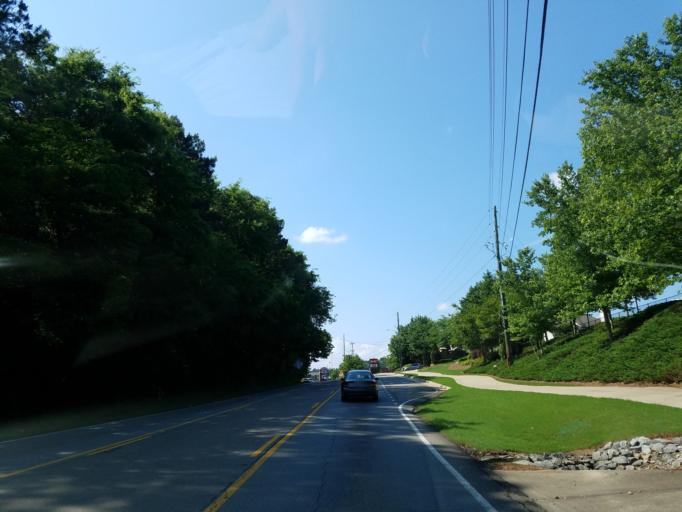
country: US
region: Georgia
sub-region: Cherokee County
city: Holly Springs
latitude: 34.1381
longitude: -84.5030
